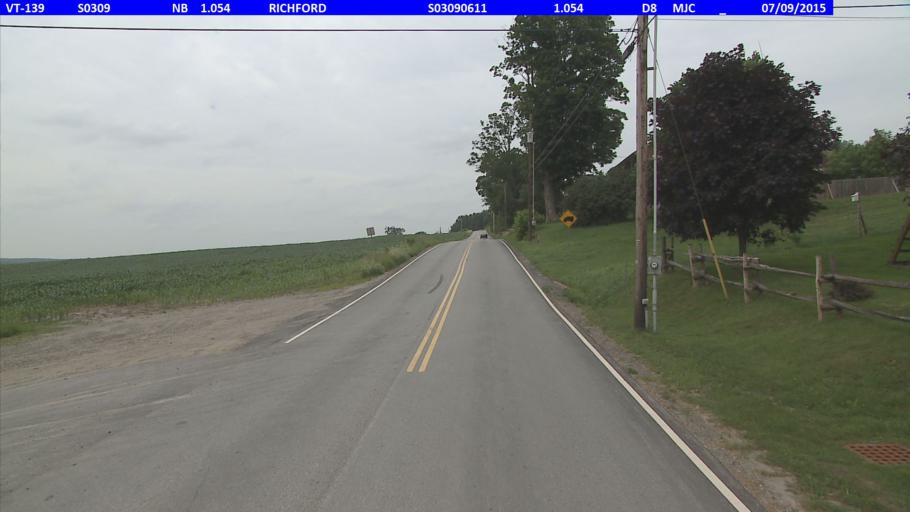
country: US
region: Vermont
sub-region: Franklin County
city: Richford
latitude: 45.0037
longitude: -72.6615
